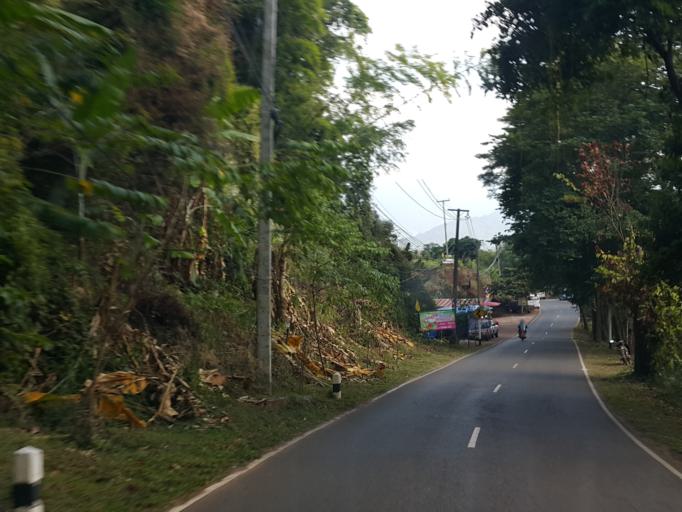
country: TH
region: Chiang Mai
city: Samoeng
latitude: 18.9131
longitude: 98.8253
